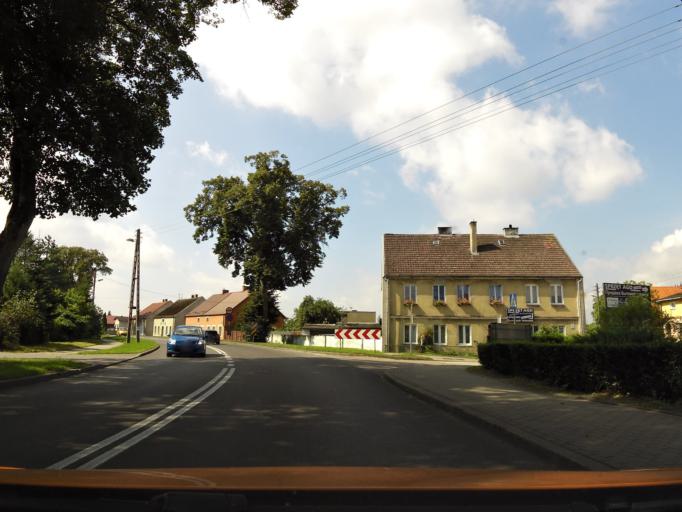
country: PL
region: West Pomeranian Voivodeship
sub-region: Powiat gryficki
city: Ploty
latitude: 53.8001
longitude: 15.2612
